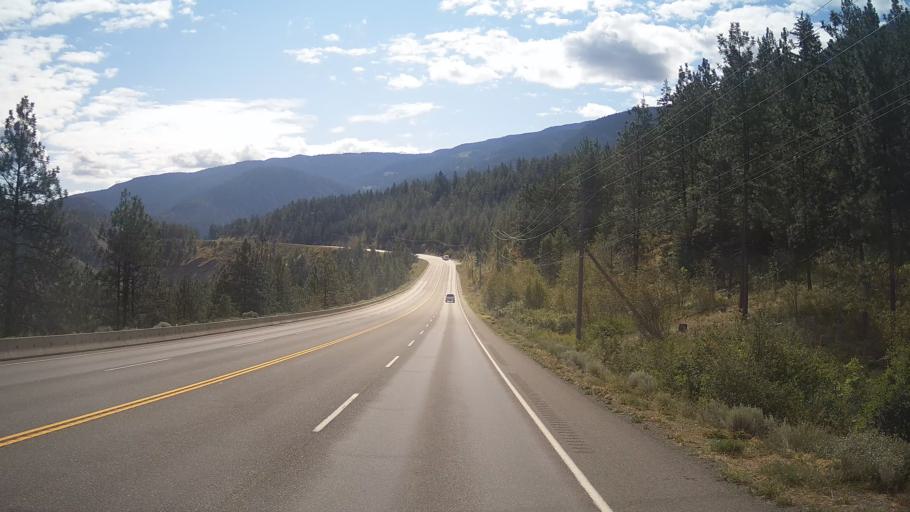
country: CA
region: British Columbia
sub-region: Thompson-Nicola Regional District
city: Ashcroft
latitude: 50.2569
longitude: -121.5245
